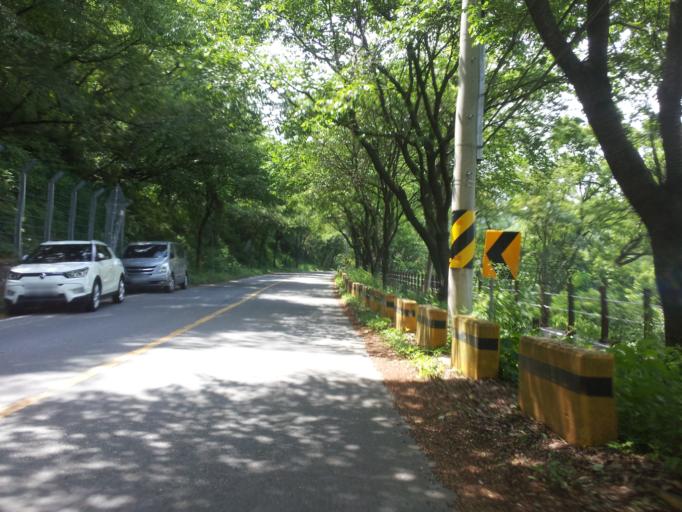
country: KR
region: Daejeon
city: Sintansin
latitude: 36.4378
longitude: 127.4705
